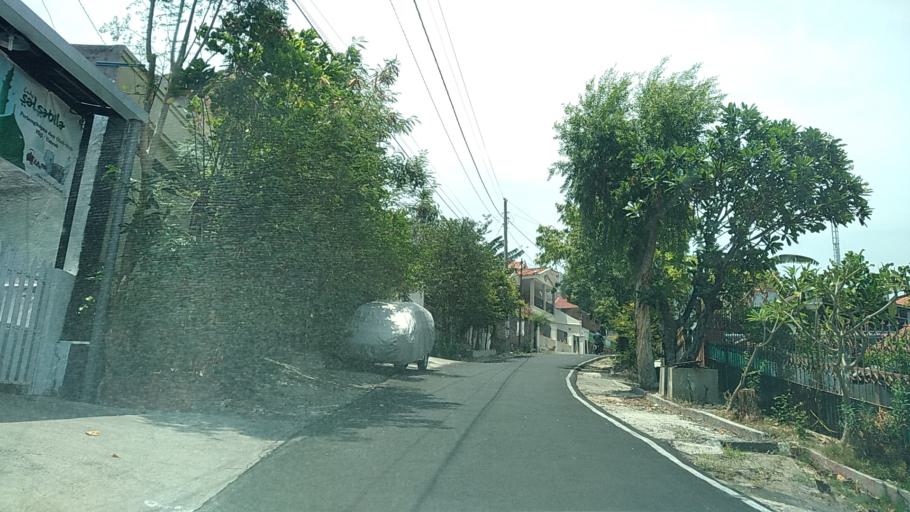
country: ID
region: Central Java
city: Semarang
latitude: -7.0113
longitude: 110.4472
